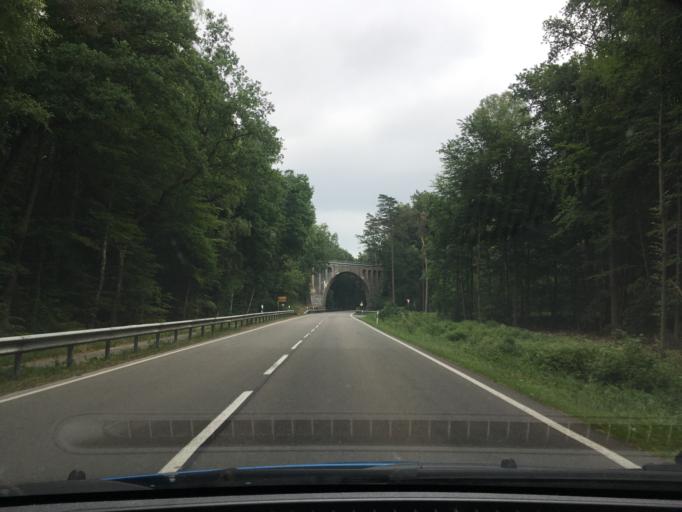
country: DE
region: Lower Saxony
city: Zernien
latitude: 53.0709
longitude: 10.9278
